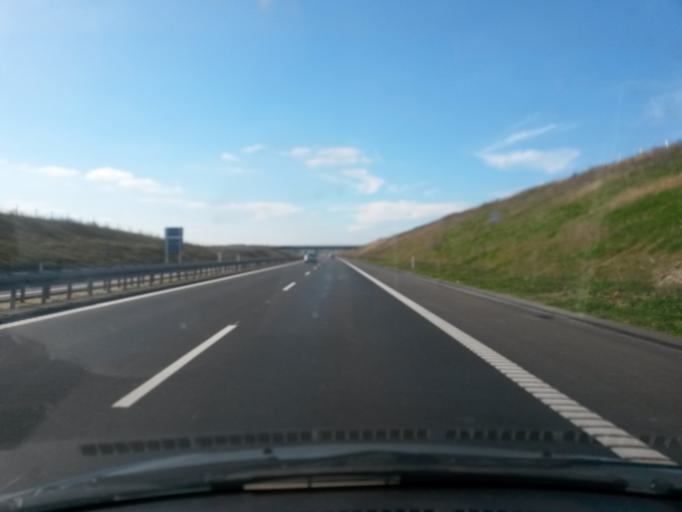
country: DK
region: Central Jutland
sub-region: Skanderborg Kommune
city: Ry
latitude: 56.1488
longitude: 9.7336
